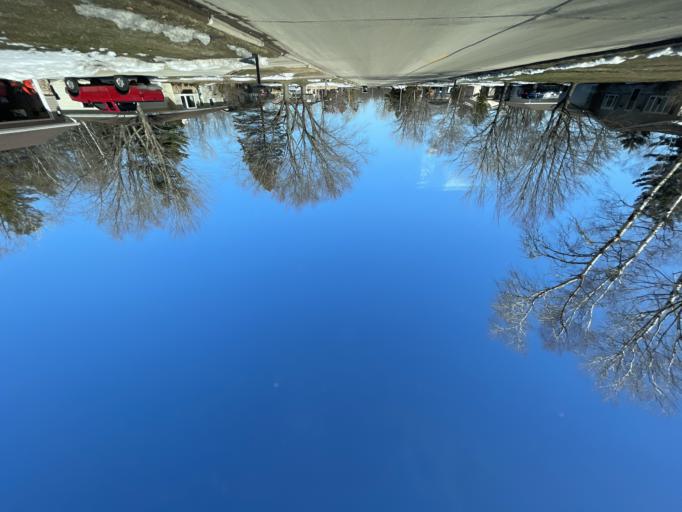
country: US
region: Wisconsin
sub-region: Brown County
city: Howard
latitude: 44.5708
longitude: -88.0804
